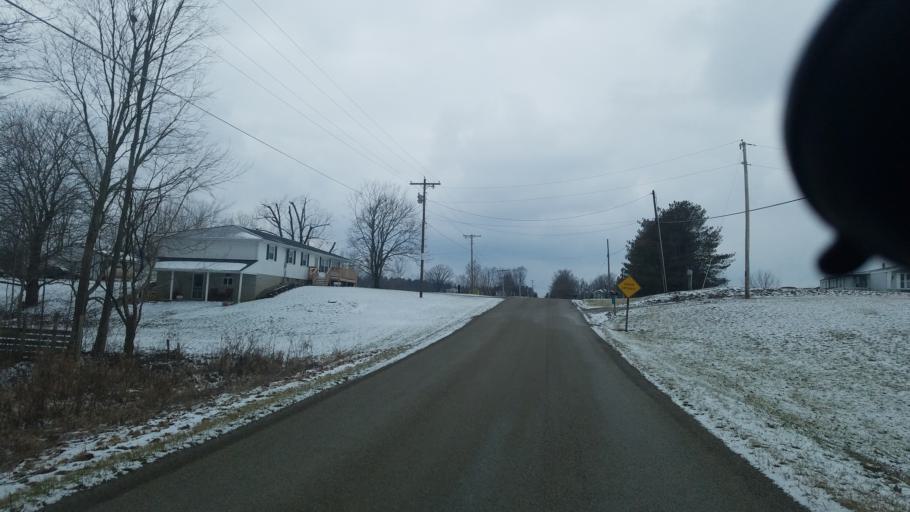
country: US
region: Ohio
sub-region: Knox County
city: Centerburg
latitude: 40.4576
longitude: -82.7012
